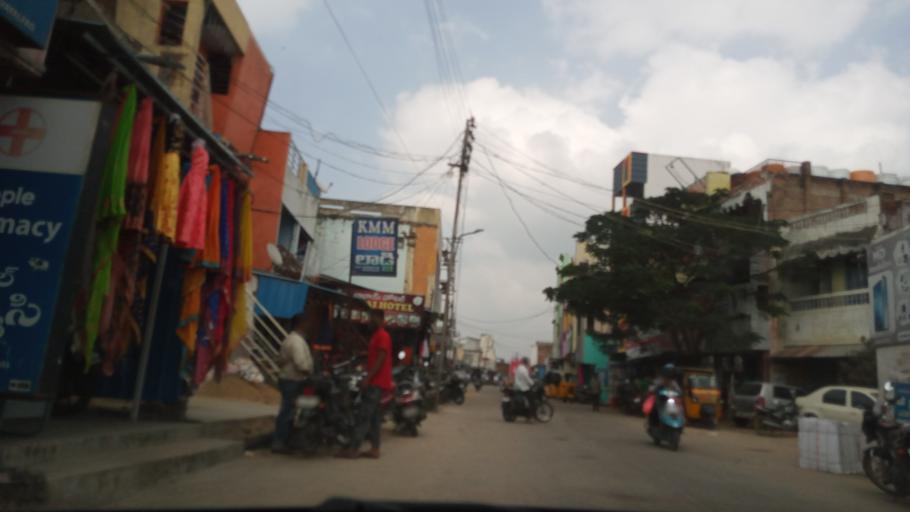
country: IN
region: Andhra Pradesh
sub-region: Chittoor
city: Madanapalle
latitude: 13.6365
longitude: 78.6296
